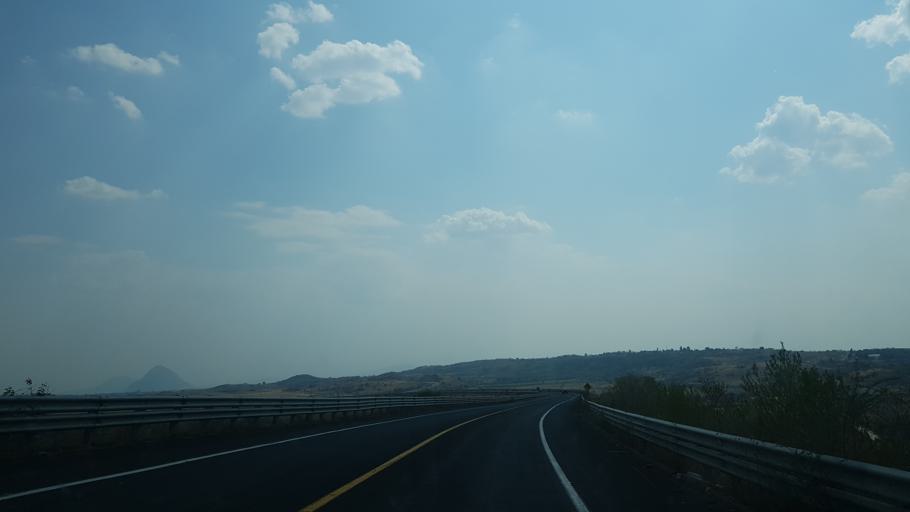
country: MX
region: Puebla
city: San Juan Amecac
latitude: 18.8202
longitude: -98.6913
